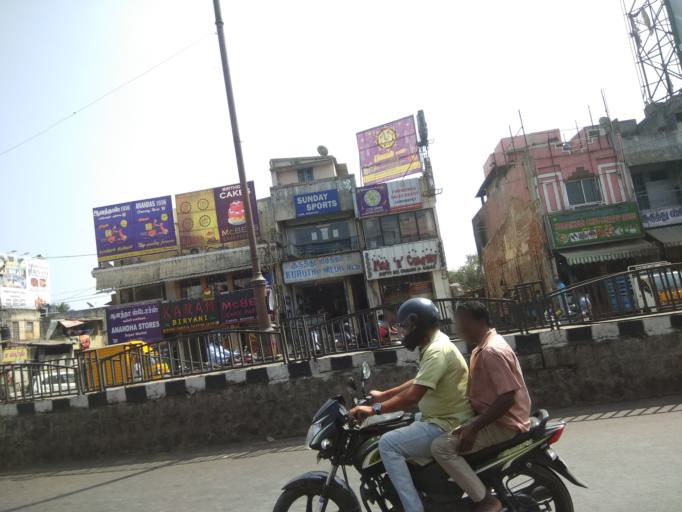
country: IN
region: Tamil Nadu
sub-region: Kancheepuram
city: Pallavaram
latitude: 12.9534
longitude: 80.1416
